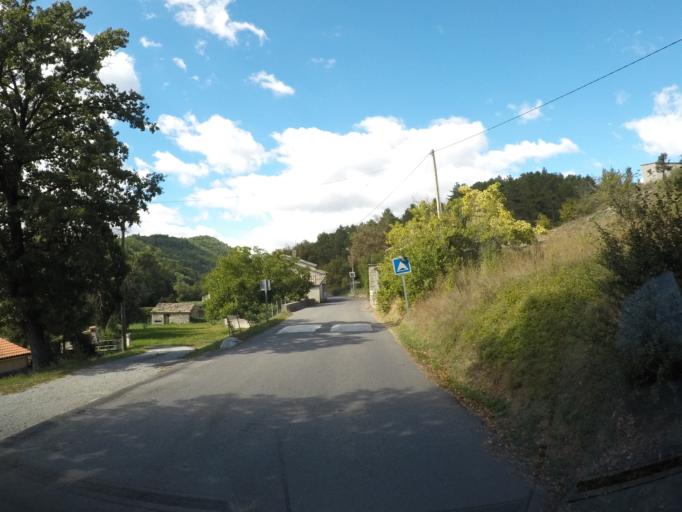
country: FR
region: Provence-Alpes-Cote d'Azur
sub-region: Departement des Hautes-Alpes
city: Laragne-Monteglin
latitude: 44.1678
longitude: 5.7479
